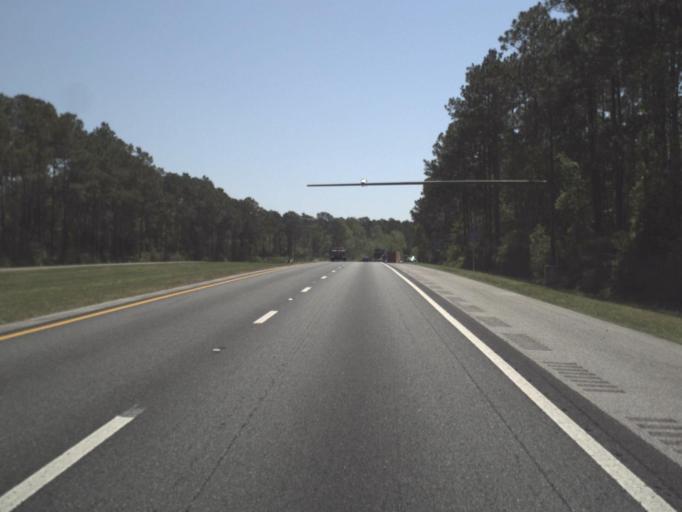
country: US
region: Florida
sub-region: Escambia County
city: Cantonment
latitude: 30.5630
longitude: -87.3786
